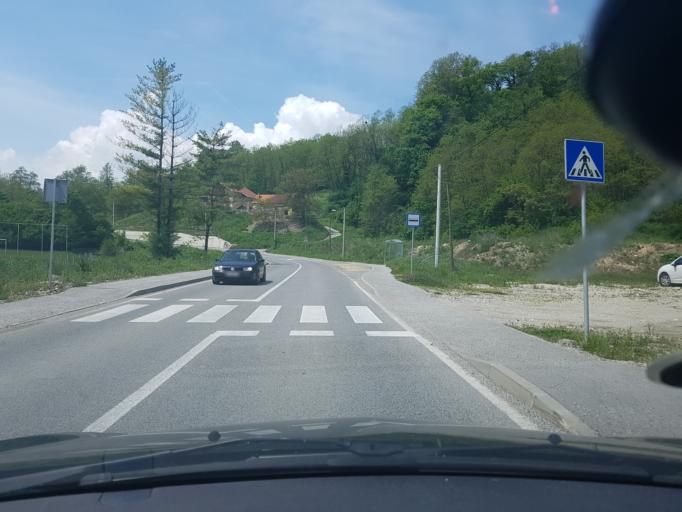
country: HR
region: Krapinsko-Zagorska
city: Pregrada
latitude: 46.1892
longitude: 15.7391
